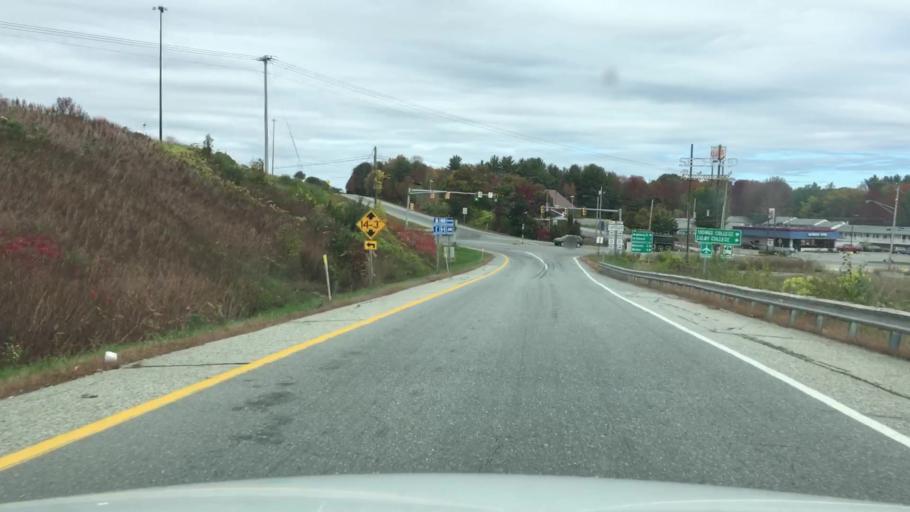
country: US
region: Maine
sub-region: Kennebec County
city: Oakland
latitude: 44.5442
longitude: -69.6799
